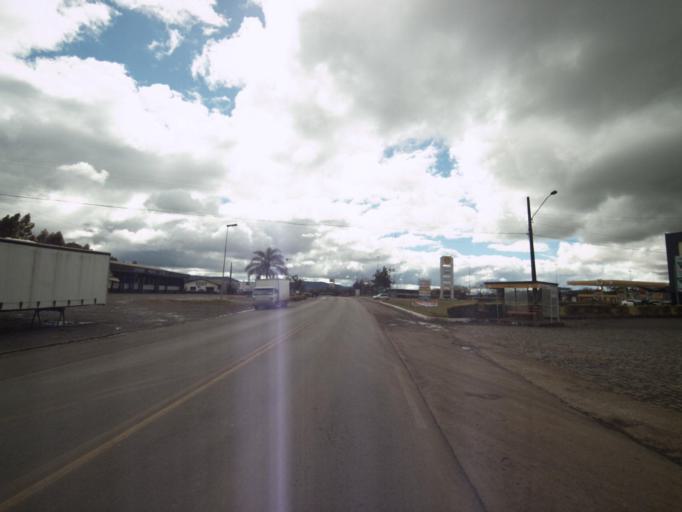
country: BR
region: Santa Catarina
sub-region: Concordia
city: Concordia
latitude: -27.2529
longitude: -51.9532
